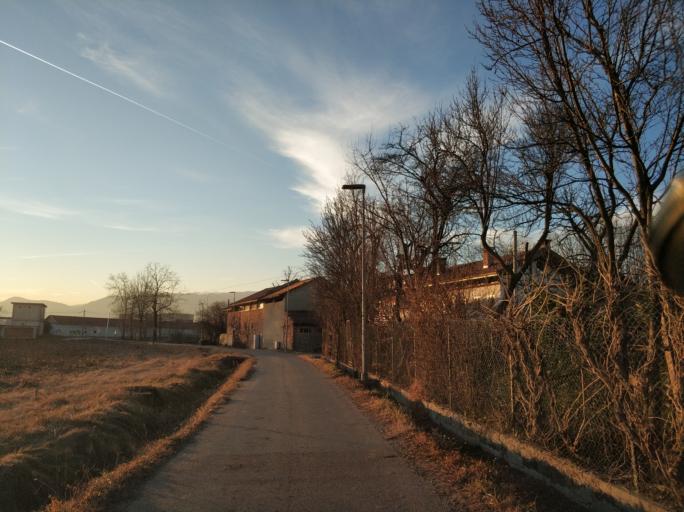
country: IT
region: Piedmont
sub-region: Provincia di Torino
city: Caselle Torinese
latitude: 45.1809
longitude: 7.6290
